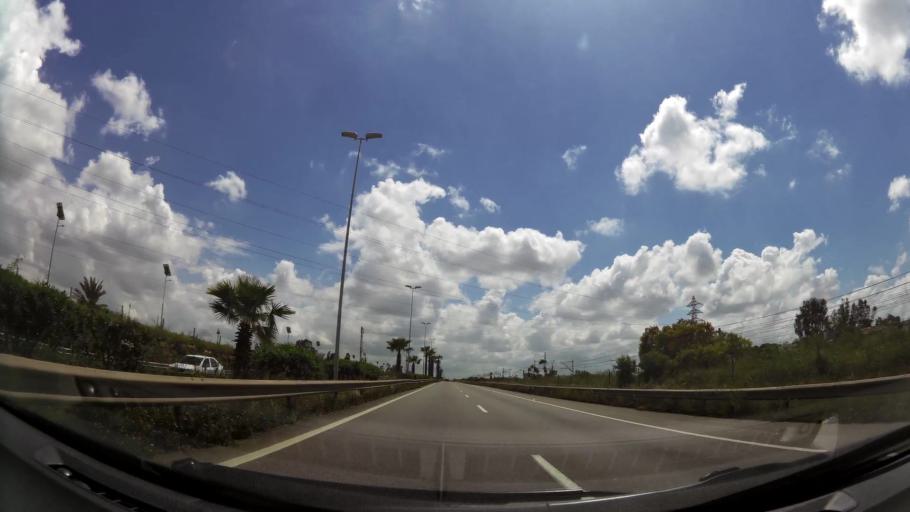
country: MA
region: Grand Casablanca
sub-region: Nouaceur
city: Bouskoura
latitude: 33.4212
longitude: -7.6271
